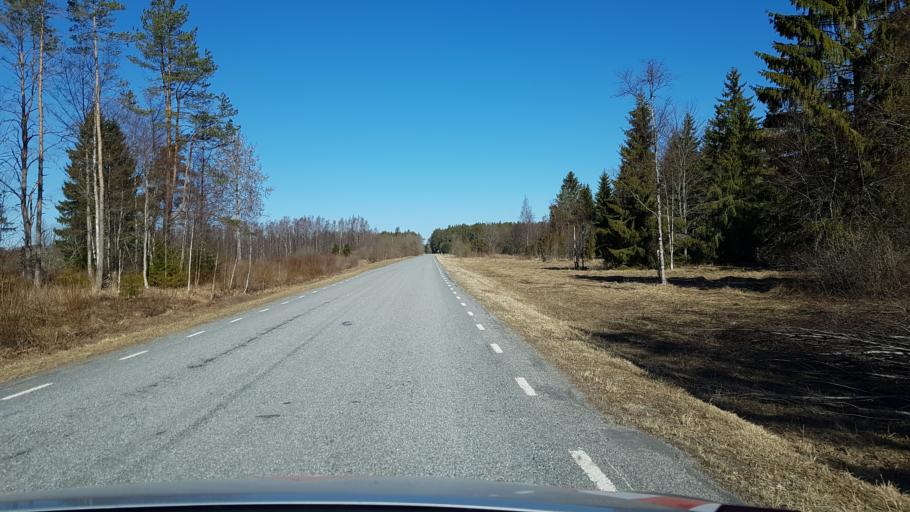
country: EE
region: Laeaene-Virumaa
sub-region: Haljala vald
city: Haljala
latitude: 59.4878
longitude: 26.2473
